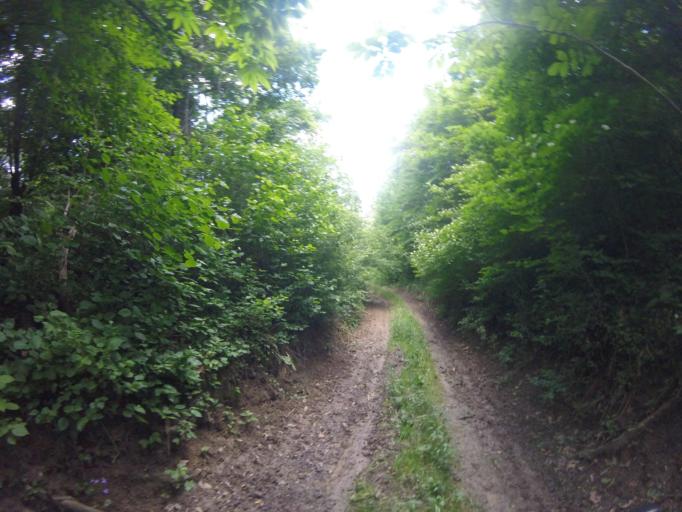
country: HU
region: Zala
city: Zalaszentgrot
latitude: 46.8963
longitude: 17.0355
